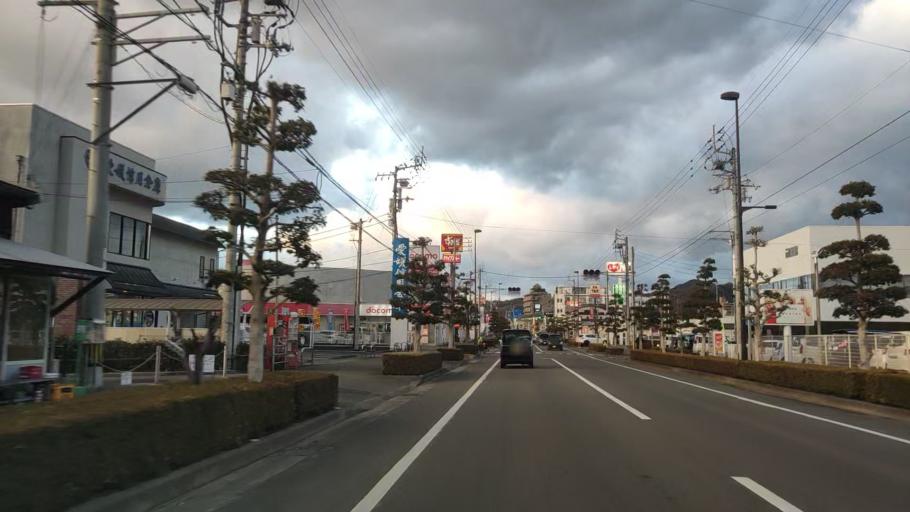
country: JP
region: Ehime
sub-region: Shikoku-chuo Shi
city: Matsuyama
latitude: 33.8352
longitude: 132.7870
